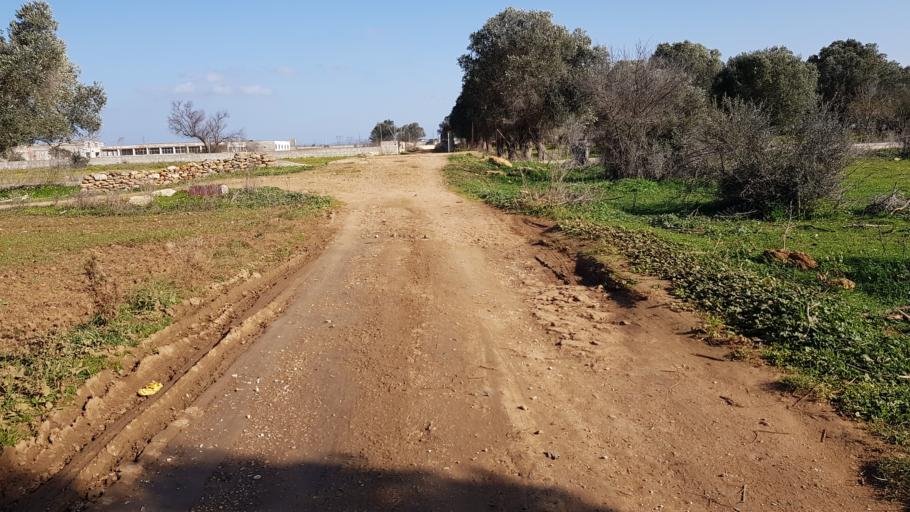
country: IT
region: Apulia
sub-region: Provincia di Brindisi
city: Mesagne
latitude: 40.5924
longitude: 17.8715
